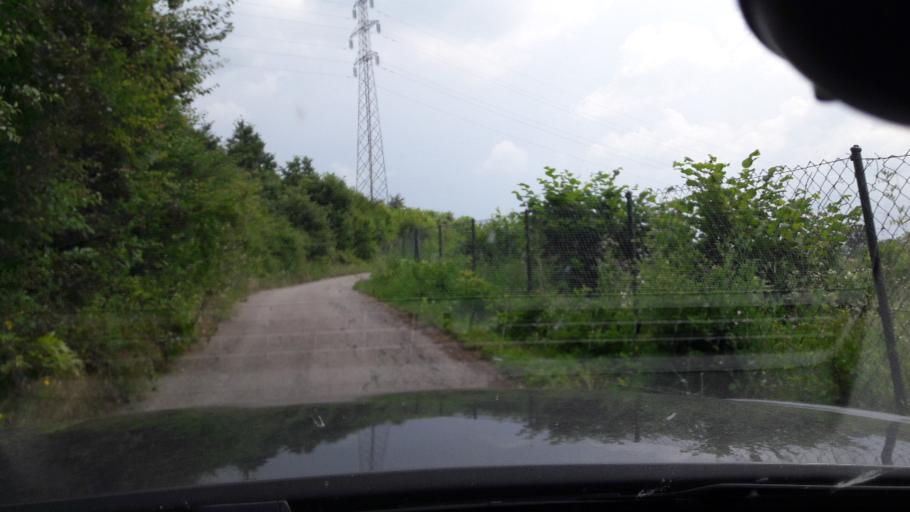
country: RS
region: Central Serbia
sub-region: Belgrade
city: Sopot
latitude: 44.6152
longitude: 20.5894
